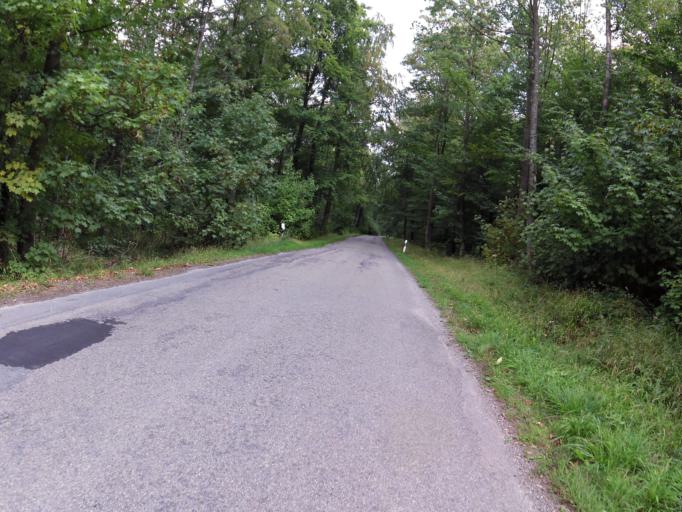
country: DE
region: North Rhine-Westphalia
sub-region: Regierungsbezirk Koln
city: Hurtgenwald
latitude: 50.7521
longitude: 6.3111
